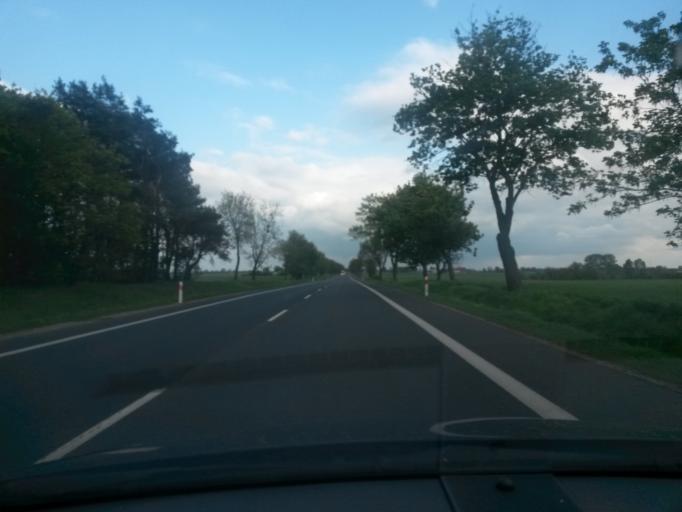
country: PL
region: Masovian Voivodeship
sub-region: Powiat sierpecki
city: Zawidz
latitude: 52.7743
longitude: 19.9191
